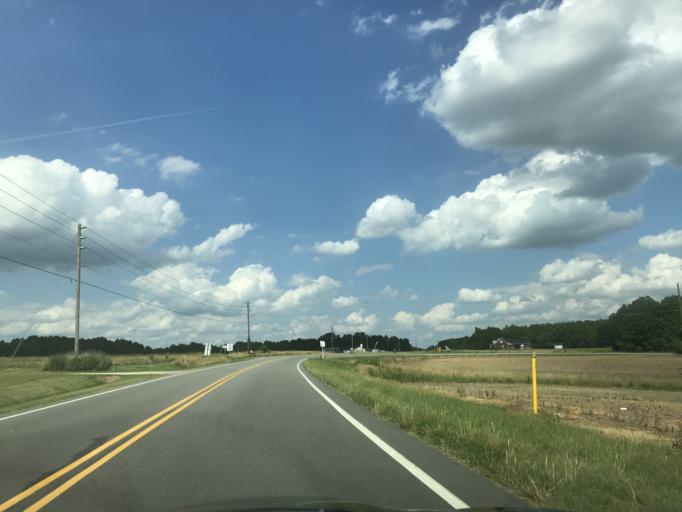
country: US
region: North Carolina
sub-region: Nash County
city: Spring Hope
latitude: 35.9592
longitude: -78.0722
